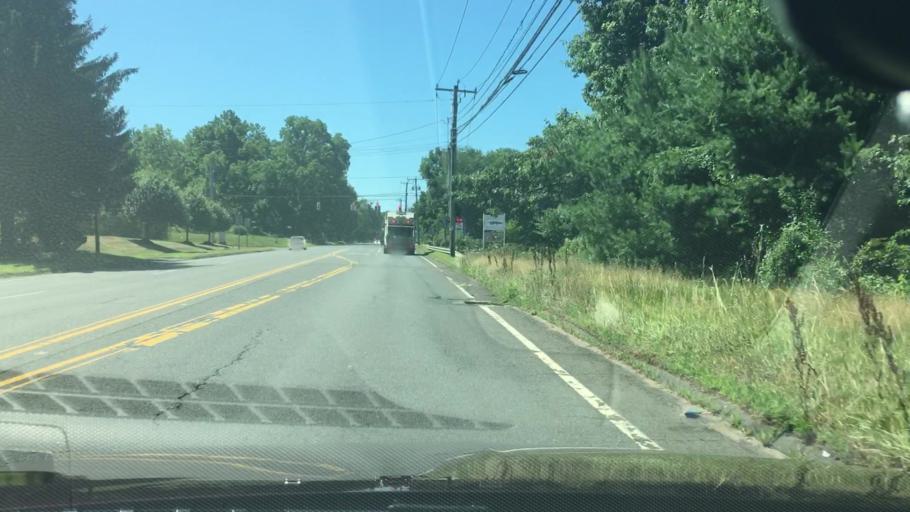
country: US
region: Connecticut
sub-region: Hartford County
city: Plainville
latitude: 41.6394
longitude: -72.9008
